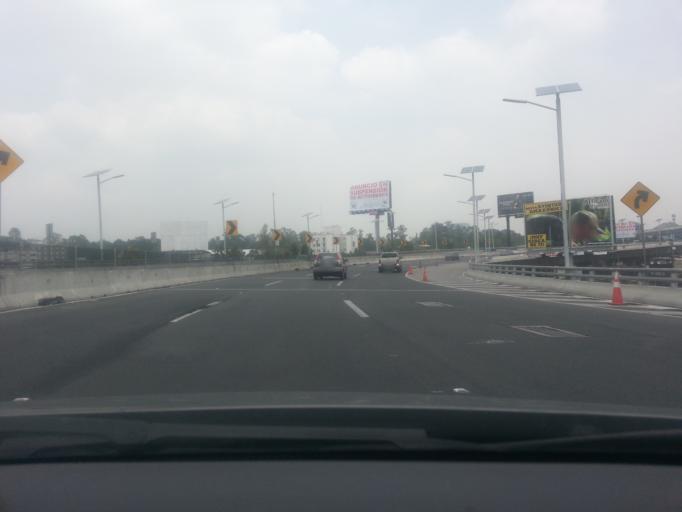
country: MX
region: Mexico City
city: Polanco
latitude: 19.4077
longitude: -99.1935
